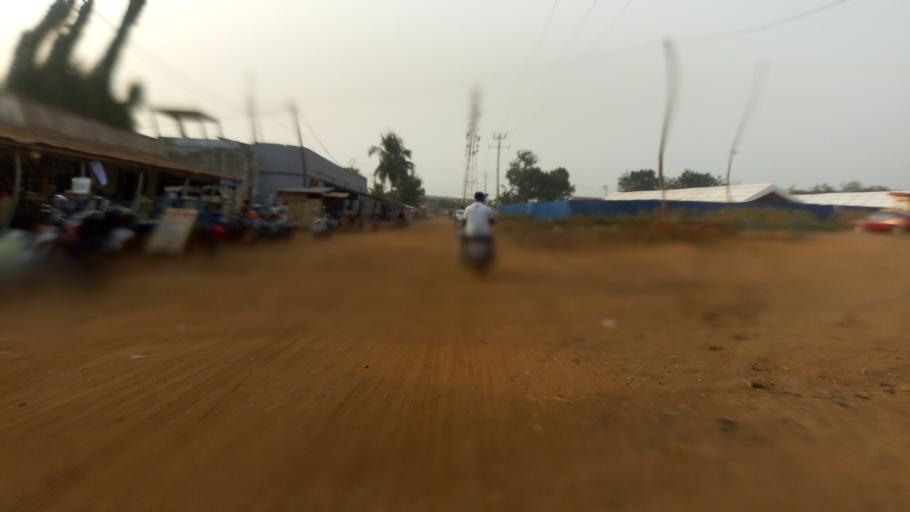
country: TG
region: Maritime
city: Tsevie
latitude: 6.3181
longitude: 1.2192
